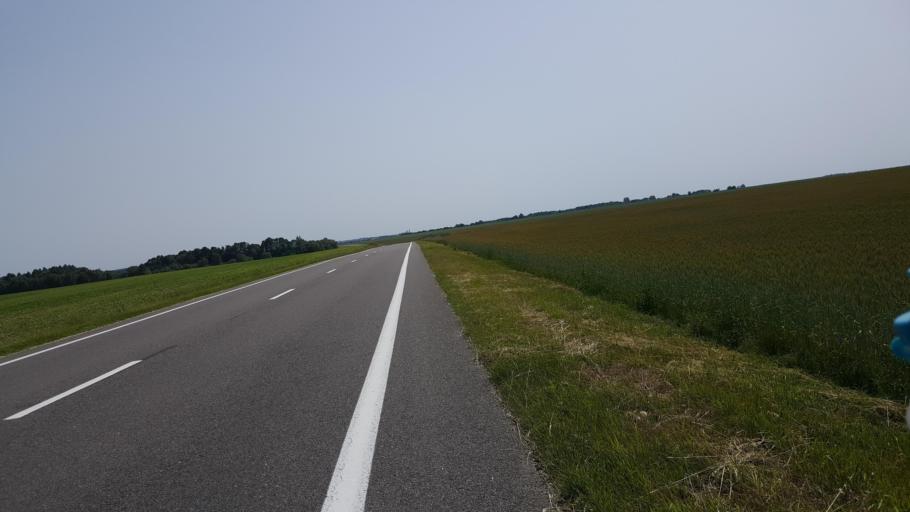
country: BY
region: Brest
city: Kamyanyets
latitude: 52.4441
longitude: 23.8322
